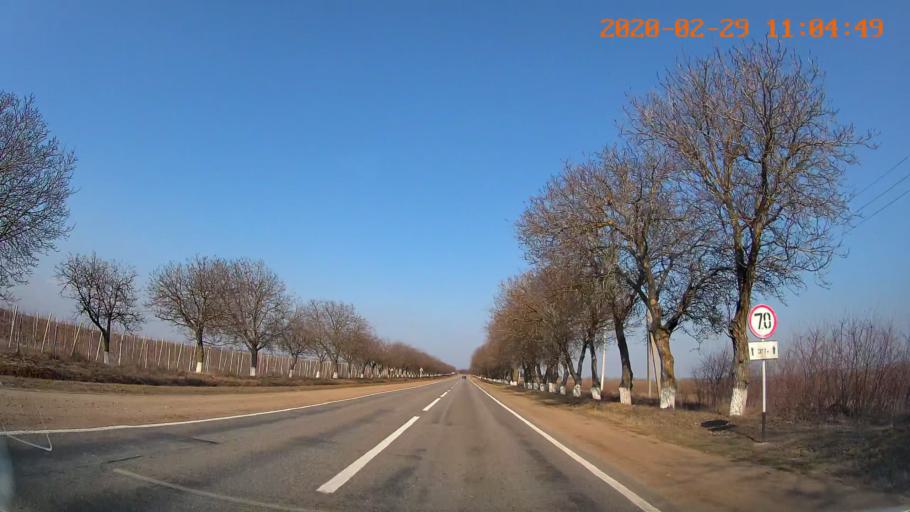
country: MD
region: Criuleni
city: Criuleni
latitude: 47.1942
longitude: 29.1977
